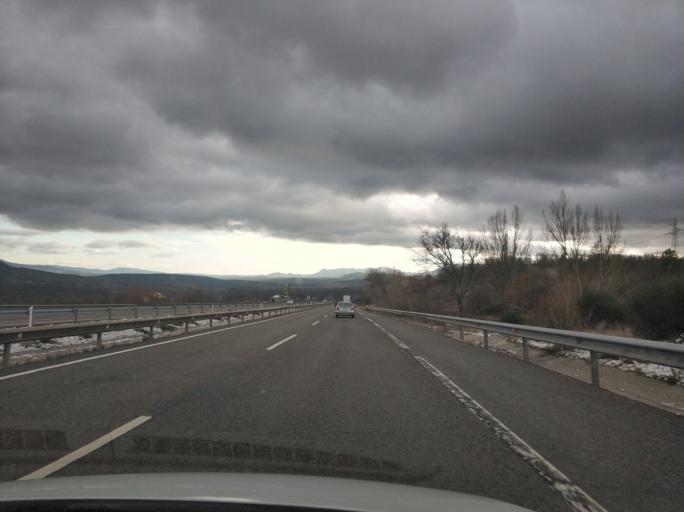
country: ES
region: Madrid
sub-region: Provincia de Madrid
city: Robregordo
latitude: 41.0932
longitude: -3.5952
